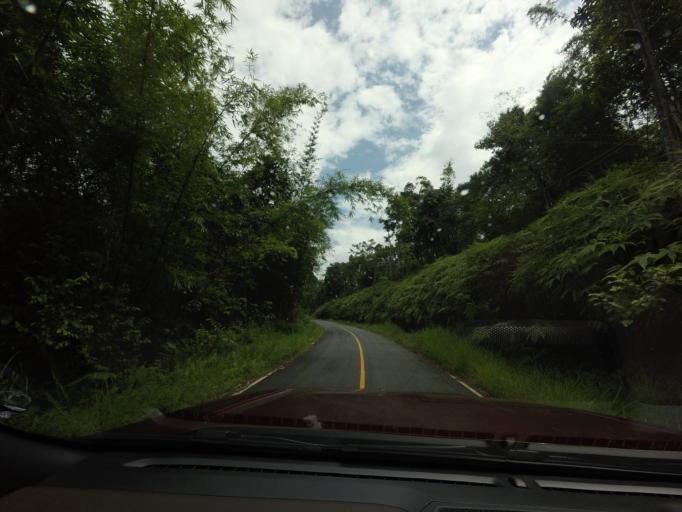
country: TH
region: Narathiwat
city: Sukhirin
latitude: 5.9464
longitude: 101.6519
